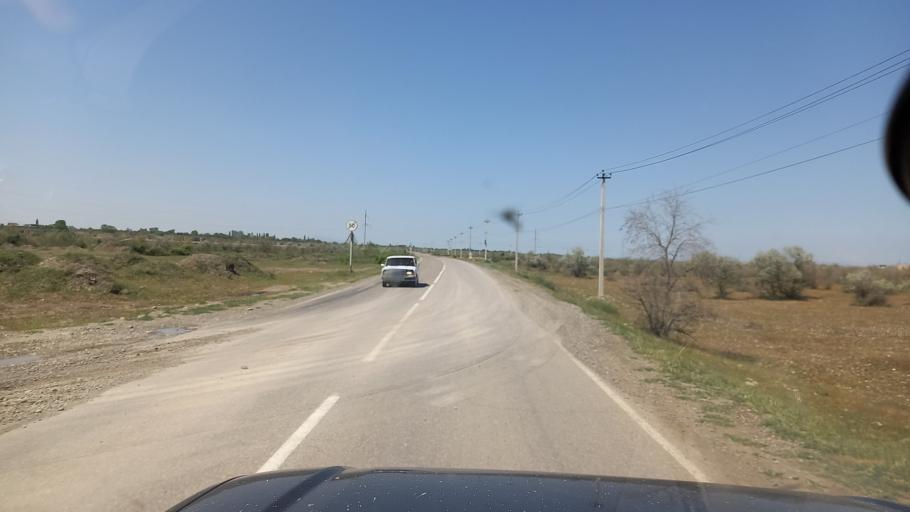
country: AZ
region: Qusar
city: Samur
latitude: 41.7294
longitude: 48.4545
